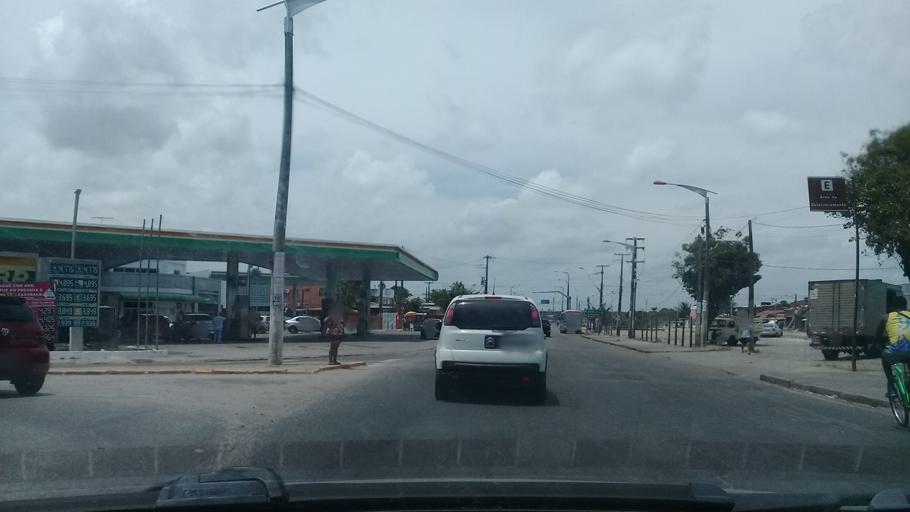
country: BR
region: Pernambuco
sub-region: Olinda
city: Olinda
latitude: -8.0201
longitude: -34.8554
